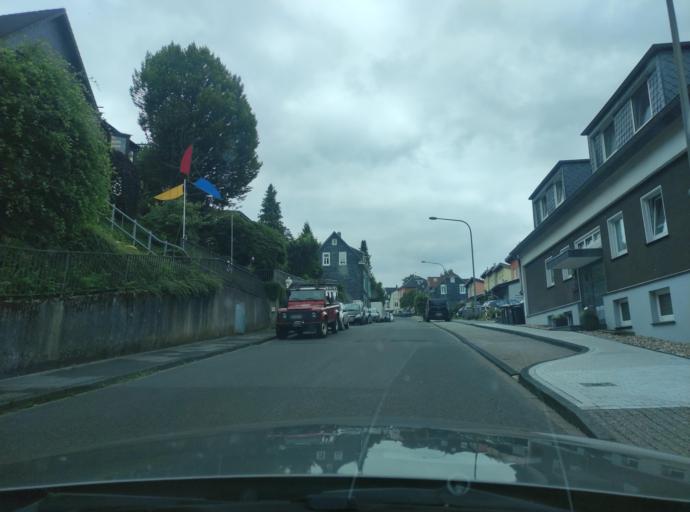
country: DE
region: North Rhine-Westphalia
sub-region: Regierungsbezirk Dusseldorf
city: Remscheid
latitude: 51.1997
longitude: 7.1658
